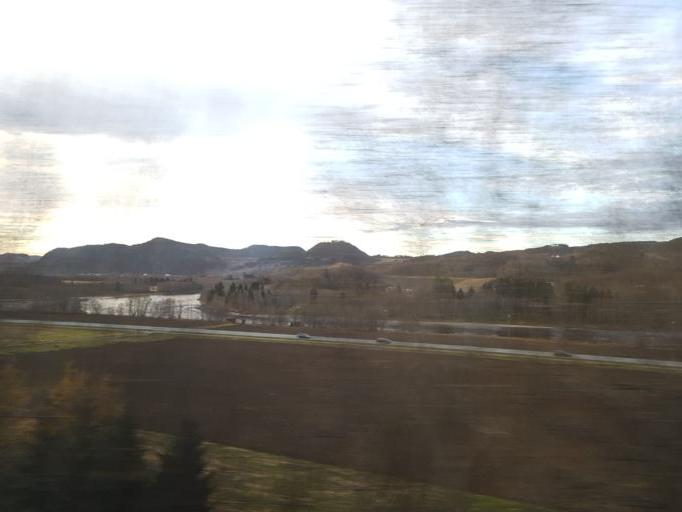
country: NO
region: Sor-Trondelag
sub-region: Melhus
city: Lundamo
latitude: 63.2094
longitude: 10.2931
